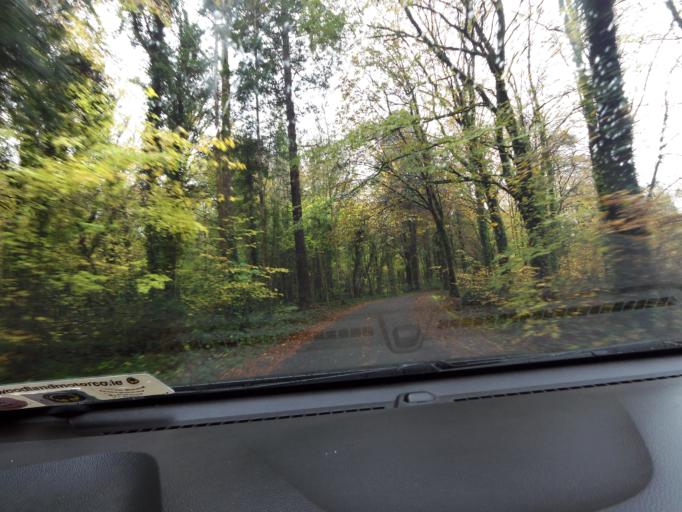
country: IE
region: Connaught
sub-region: County Galway
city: Gort
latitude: 53.0936
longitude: -8.8365
